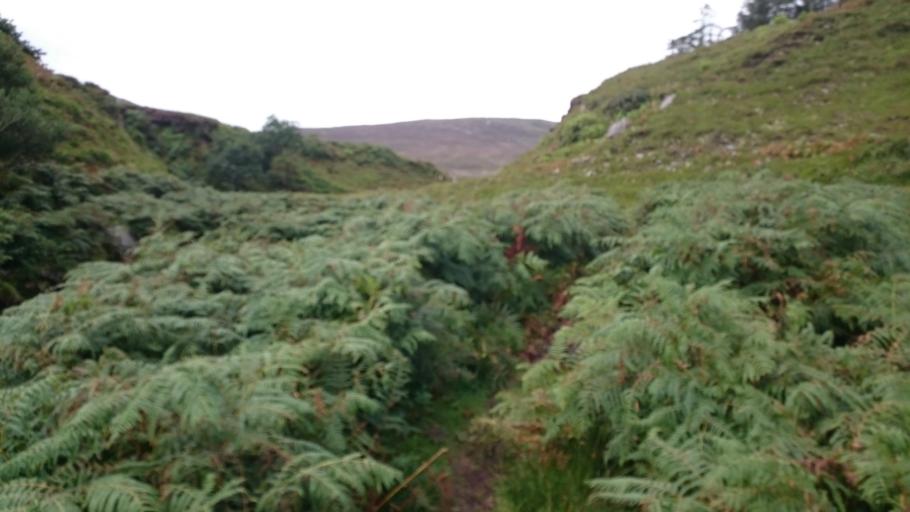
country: IE
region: Connaught
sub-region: Maigh Eo
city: Westport
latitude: 53.9890
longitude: -9.5832
